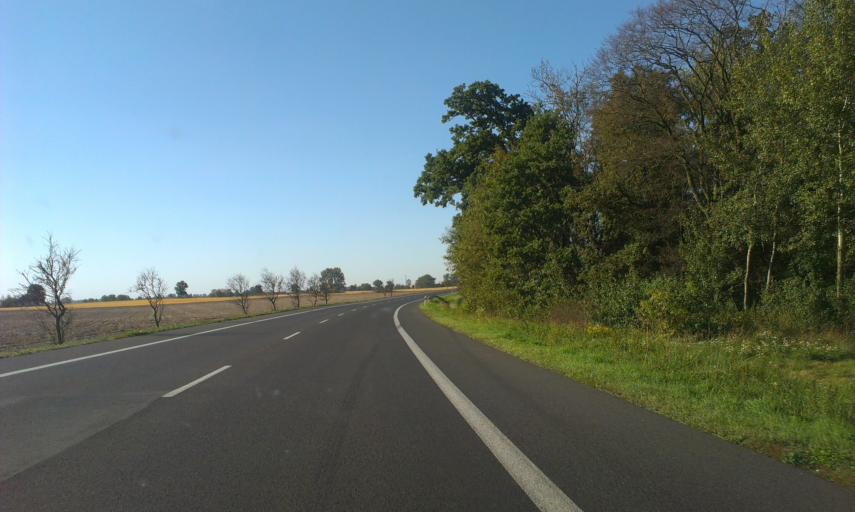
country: PL
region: Kujawsko-Pomorskie
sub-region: Powiat torunski
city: Chelmza
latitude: 53.1723
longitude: 18.5734
